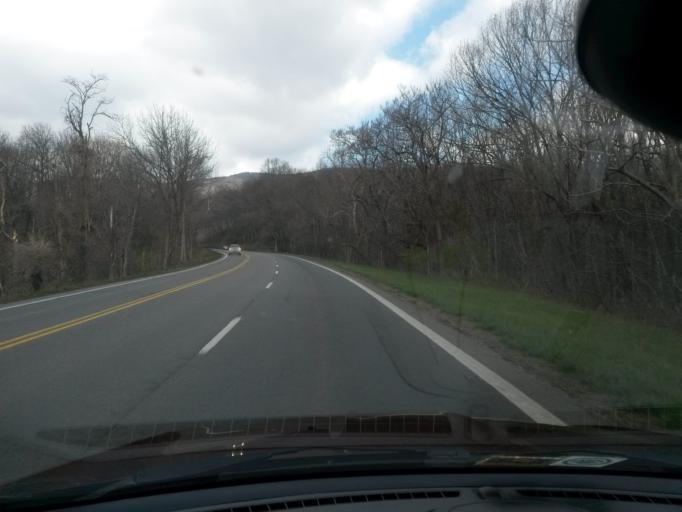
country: US
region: Virginia
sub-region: City of Waynesboro
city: Waynesboro
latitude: 38.0365
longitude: -78.8139
